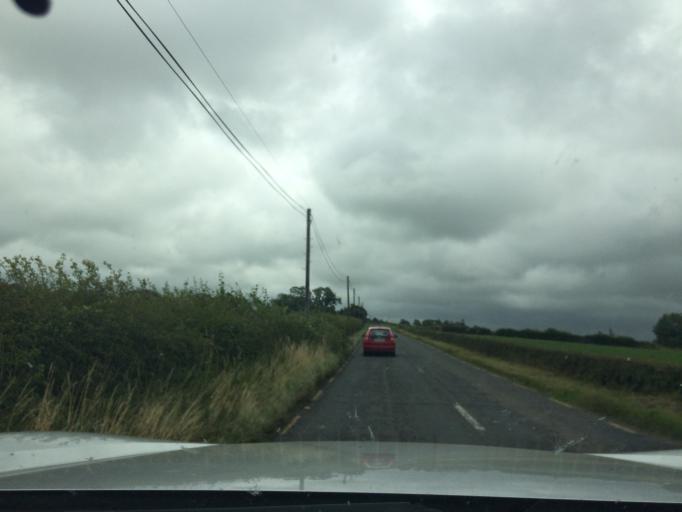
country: IE
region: Munster
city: Cashel
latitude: 52.4921
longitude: -7.8618
